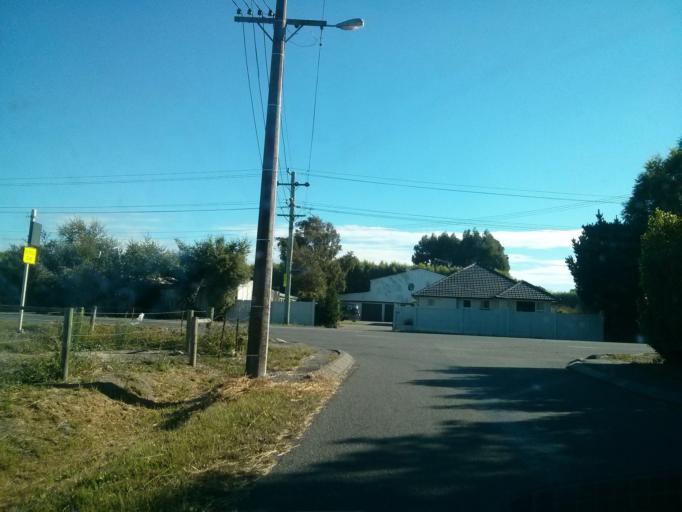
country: NZ
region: Canterbury
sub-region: Christchurch City
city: Christchurch
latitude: -43.4800
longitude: 172.5623
